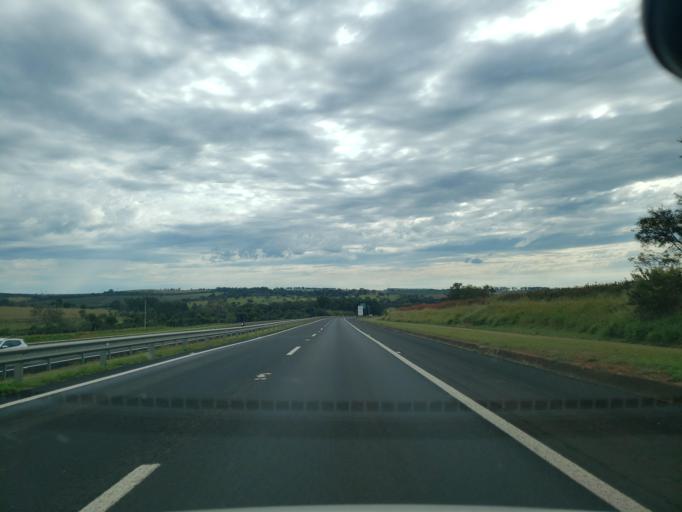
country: BR
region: Sao Paulo
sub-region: Bauru
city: Bauru
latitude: -22.2130
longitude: -49.1763
